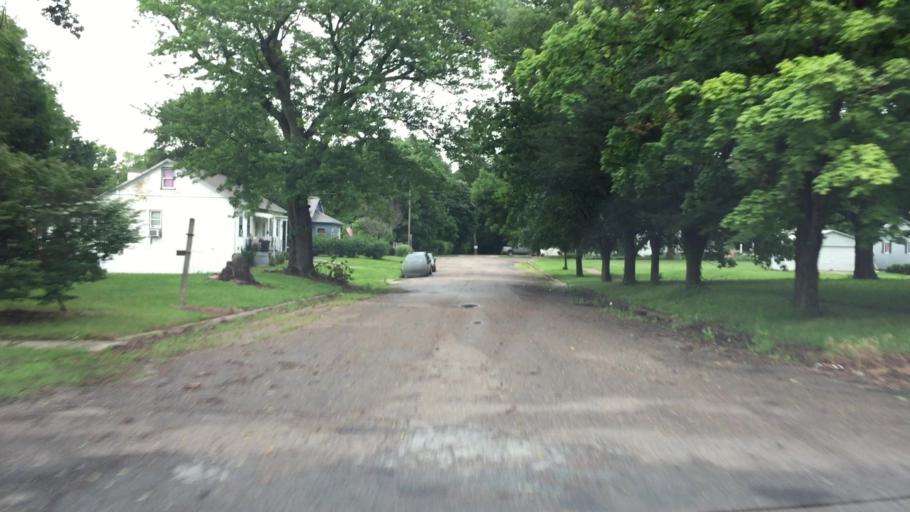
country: US
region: Illinois
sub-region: Hancock County
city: Warsaw
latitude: 40.3613
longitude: -91.4391
